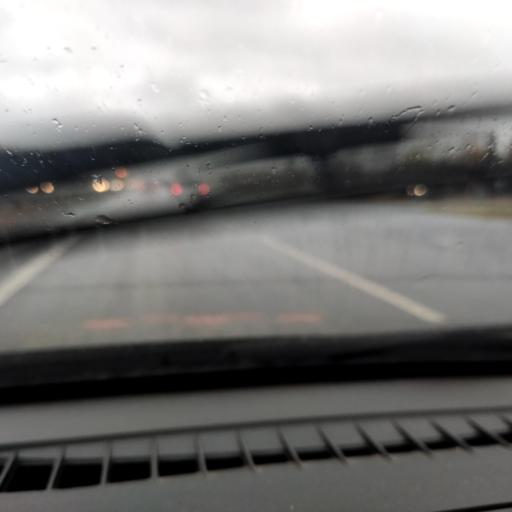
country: RU
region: Samara
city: Tol'yatti
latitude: 53.5773
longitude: 49.4232
